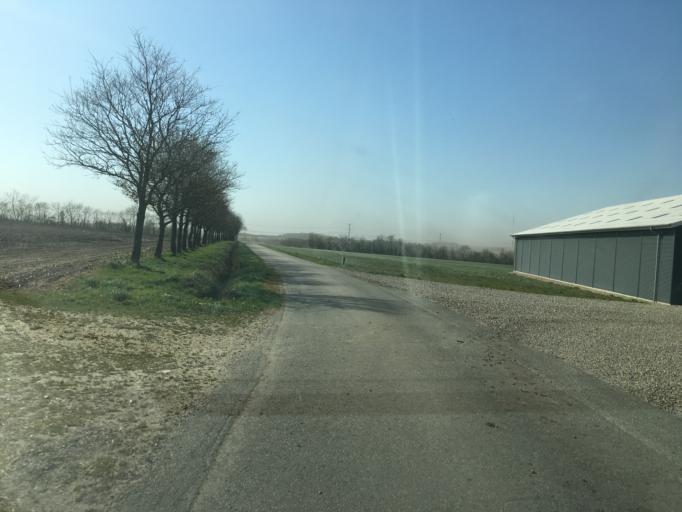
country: DK
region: South Denmark
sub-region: Aabenraa Kommune
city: Rodekro
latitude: 55.1065
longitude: 9.2315
